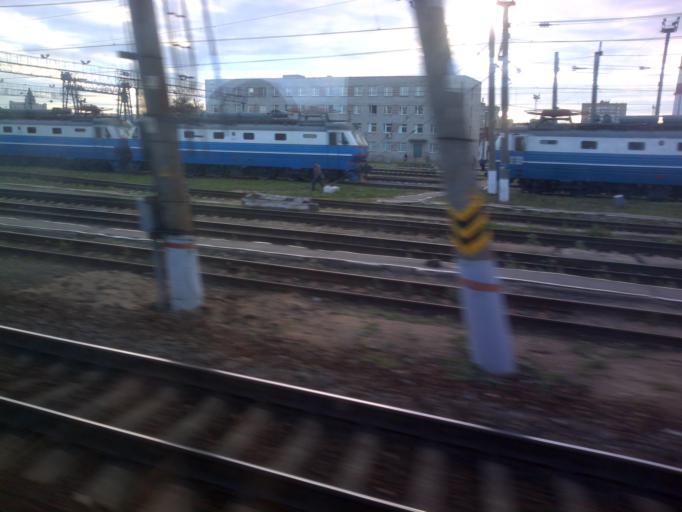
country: RU
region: Moscow
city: Zamoskvorech'ye
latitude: 55.7165
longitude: 37.6428
